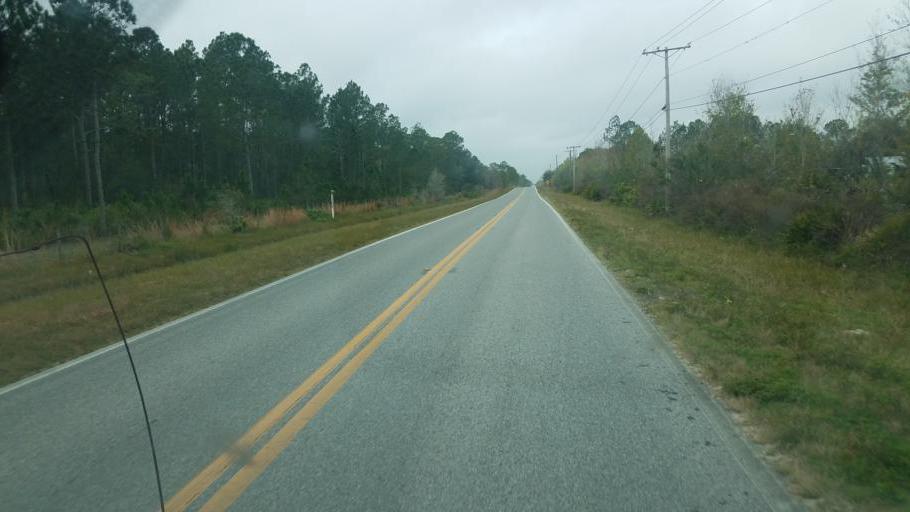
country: US
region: Florida
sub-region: Polk County
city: Polk City
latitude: 28.2591
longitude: -81.8744
